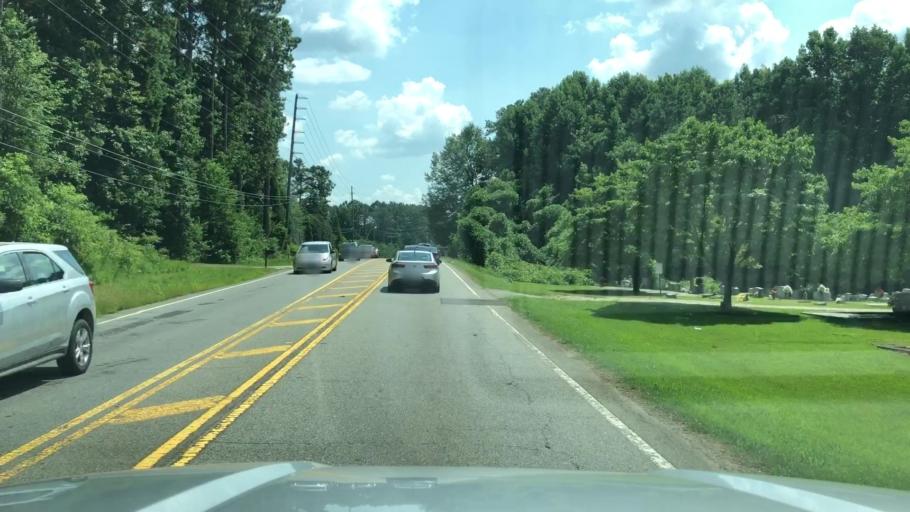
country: US
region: Georgia
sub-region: Cobb County
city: Acworth
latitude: 33.9940
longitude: -84.7074
